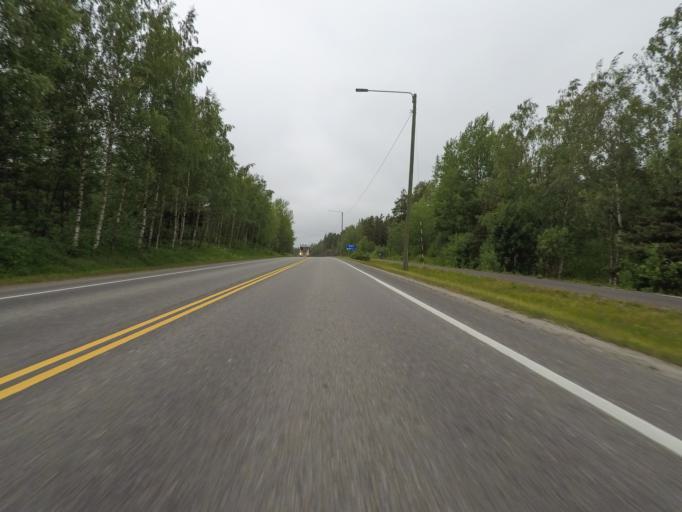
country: FI
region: Varsinais-Suomi
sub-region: Turku
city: Raisio
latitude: 60.4661
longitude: 22.0994
